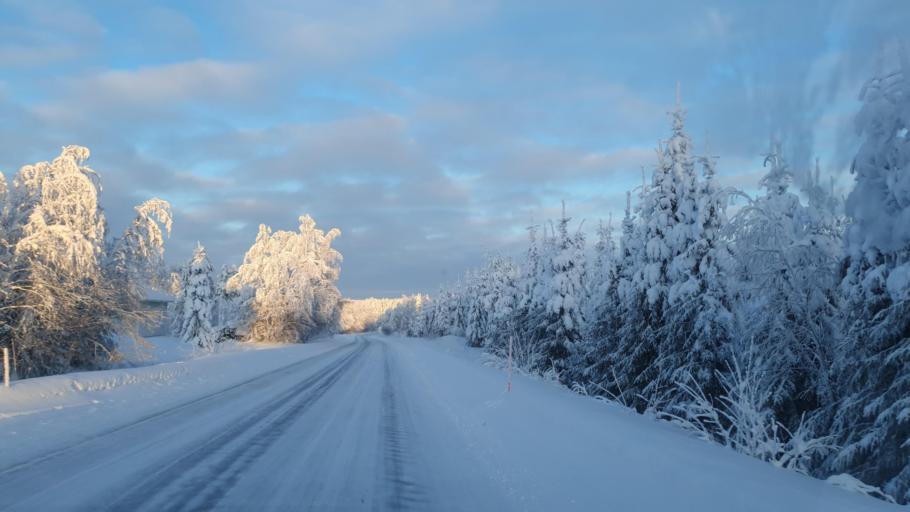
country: FI
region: Kainuu
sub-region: Kajaani
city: Vuokatti
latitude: 64.2526
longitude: 28.2327
